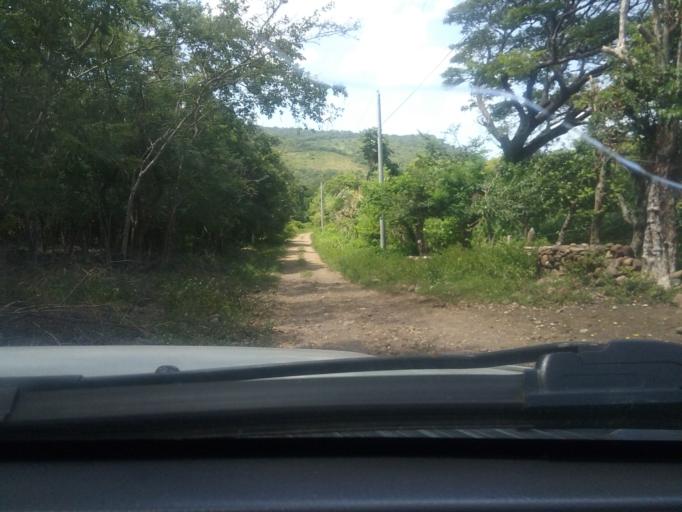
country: NI
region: Matagalpa
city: Terrabona
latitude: 12.6512
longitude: -85.9946
